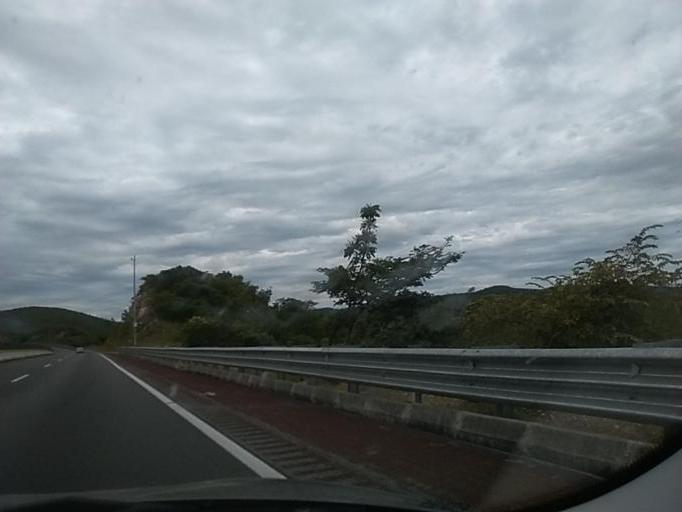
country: MX
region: Guerrero
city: Copalillo
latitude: 18.0908
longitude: -99.2242
